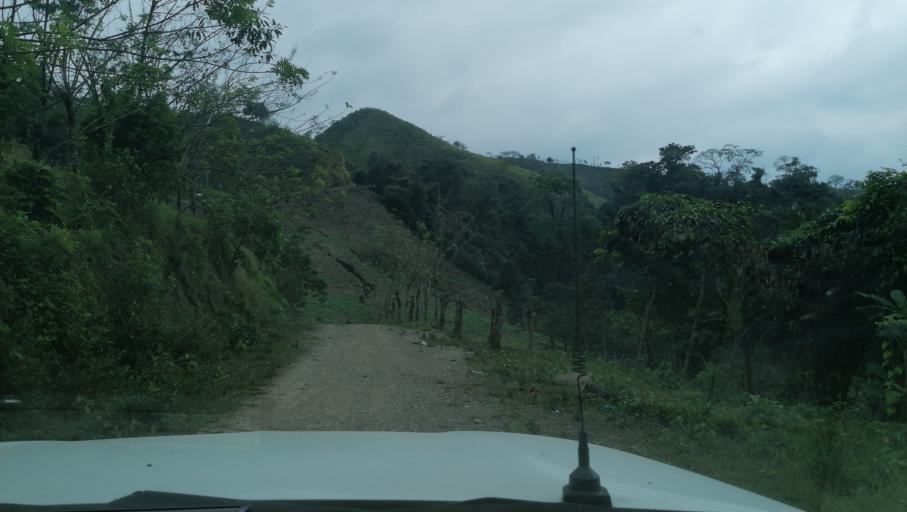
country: MX
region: Chiapas
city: Ostuacan
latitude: 17.3496
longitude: -93.3092
